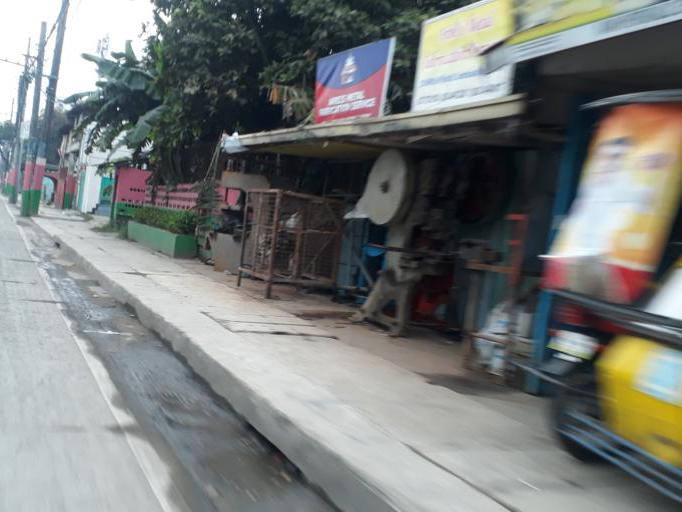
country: PH
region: Calabarzon
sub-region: Province of Rizal
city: Valenzuela
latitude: 14.6898
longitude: 120.9565
